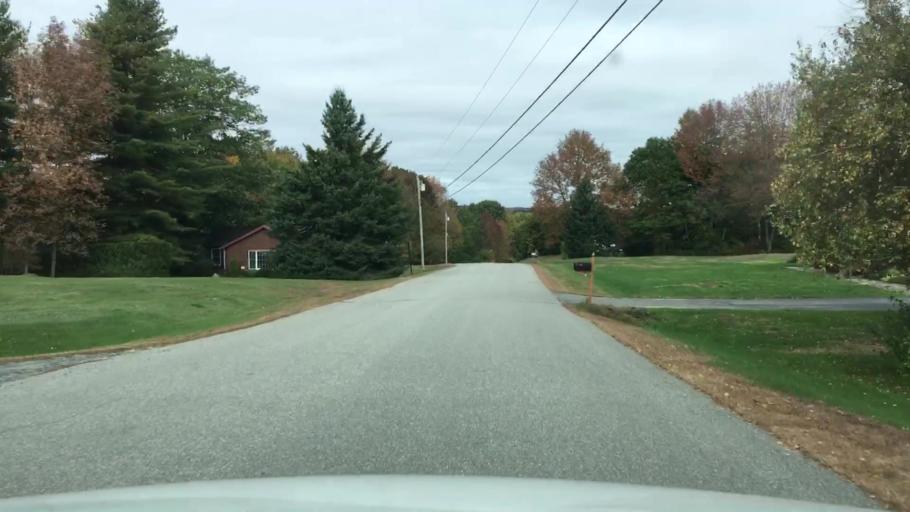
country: US
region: Maine
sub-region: Kennebec County
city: Oakland
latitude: 44.5635
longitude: -69.6807
